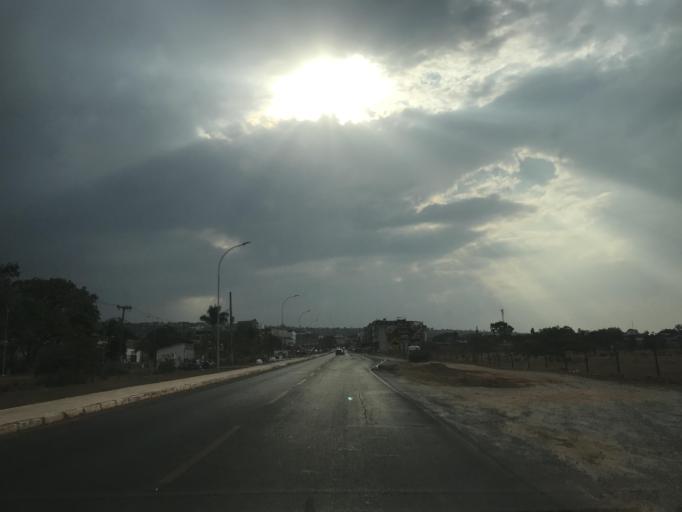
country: BR
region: Federal District
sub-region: Brasilia
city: Brasilia
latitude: -15.6625
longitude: -47.8318
